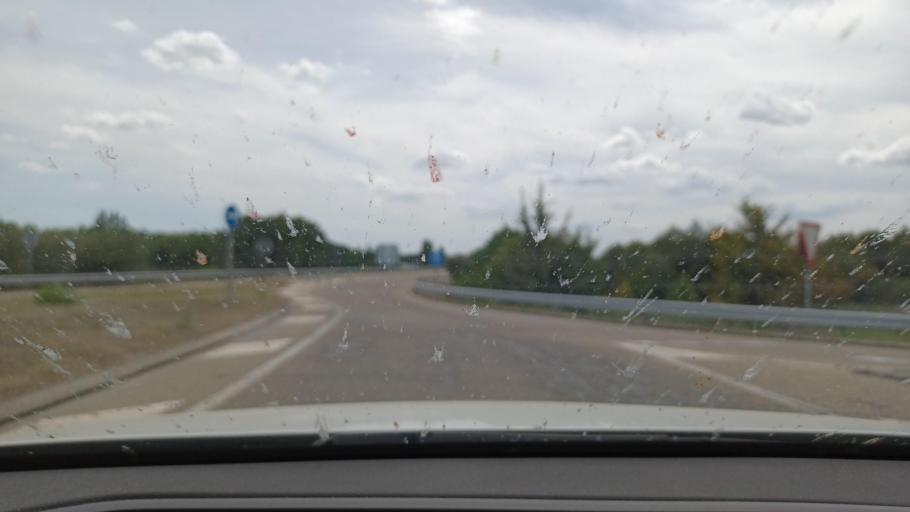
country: ES
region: Castille and Leon
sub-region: Provincia de Segovia
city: Cuellar
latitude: 41.3876
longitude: -4.2933
